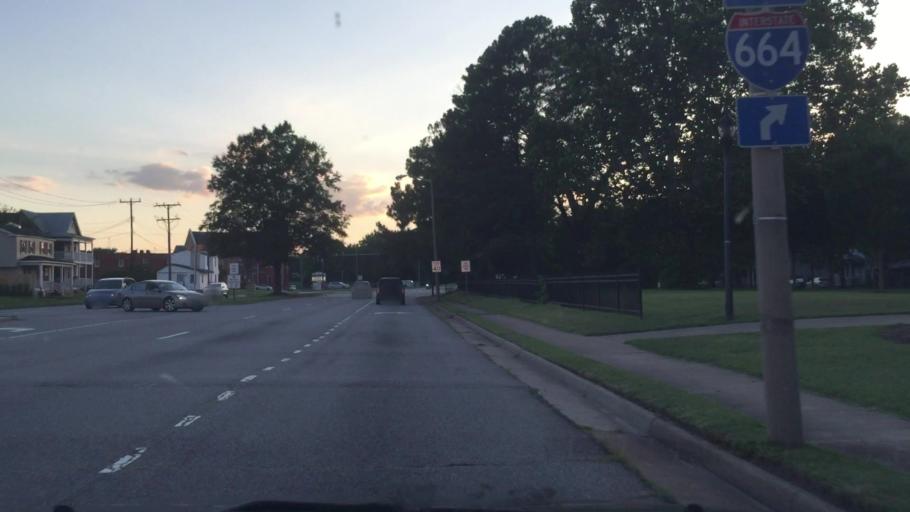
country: US
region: Virginia
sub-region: City of Portsmouth
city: Portsmouth
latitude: 36.8376
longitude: -76.3238
